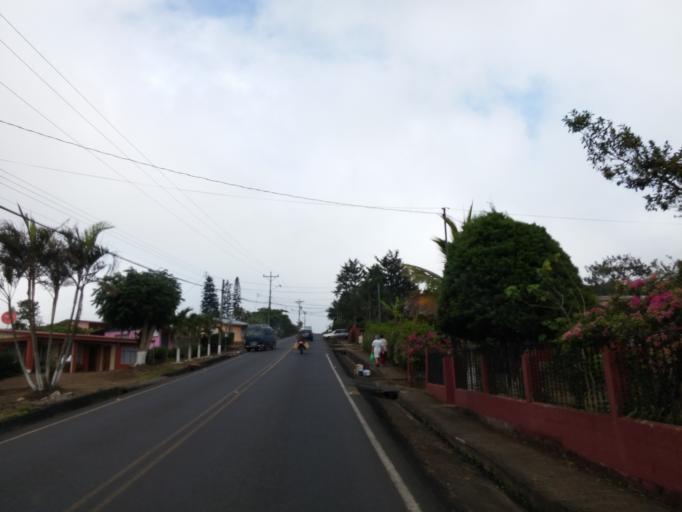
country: CR
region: Alajuela
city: San Ramon
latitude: 10.1273
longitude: -84.4719
